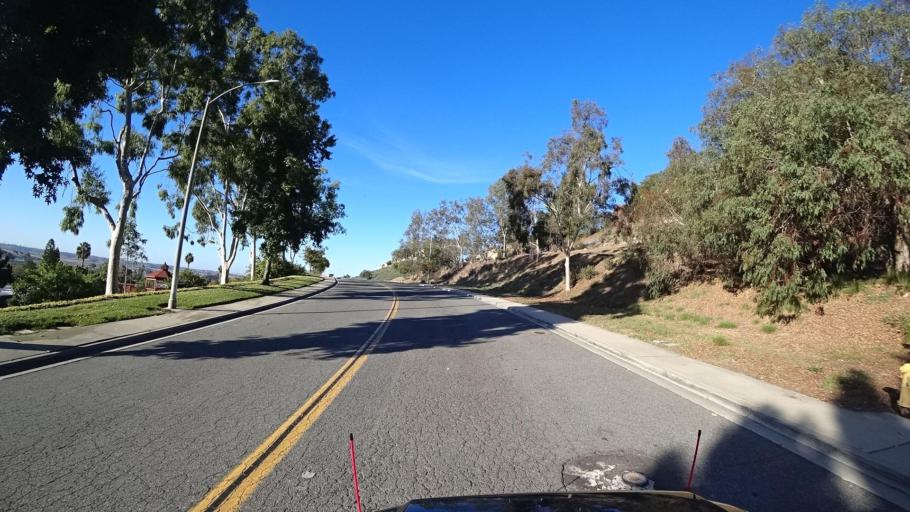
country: US
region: California
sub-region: San Diego County
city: La Presa
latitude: 32.7133
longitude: -116.9833
